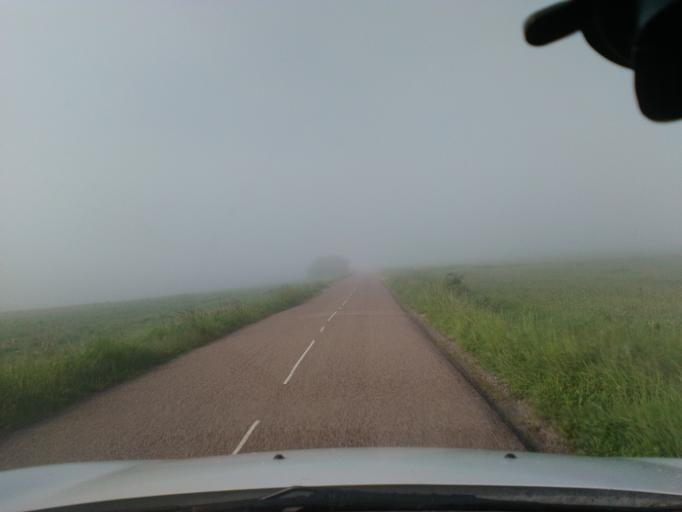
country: FR
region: Lorraine
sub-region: Departement des Vosges
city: Charmes
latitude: 48.3452
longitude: 6.2383
